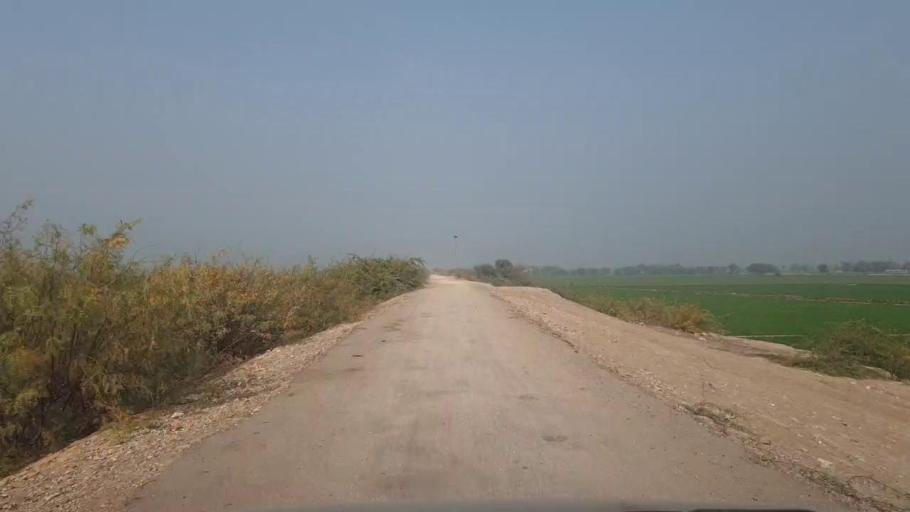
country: PK
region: Sindh
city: Hala
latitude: 25.8136
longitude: 68.4013
